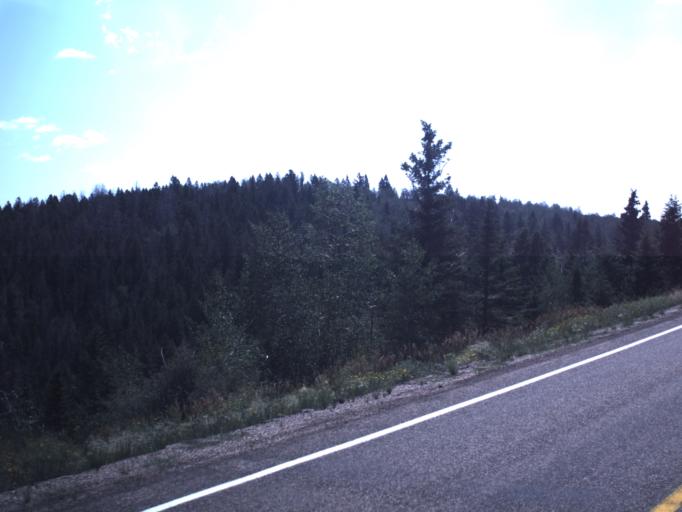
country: US
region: Utah
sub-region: Uintah County
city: Maeser
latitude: 40.7010
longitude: -109.4925
